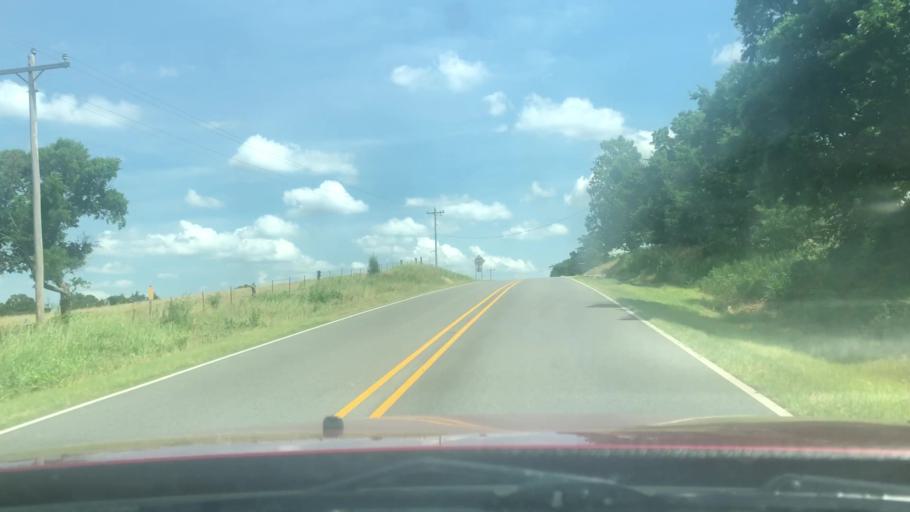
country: US
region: Arkansas
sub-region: Carroll County
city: Berryville
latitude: 36.3952
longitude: -93.5478
